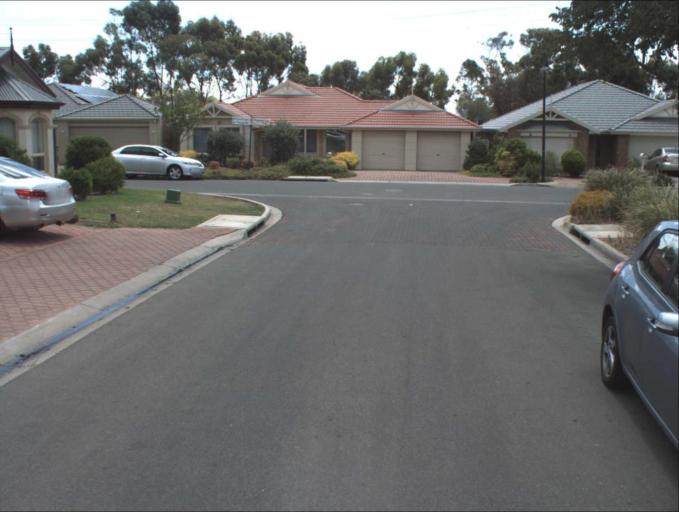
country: AU
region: South Australia
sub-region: Salisbury
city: Ingle Farm
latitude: -34.8481
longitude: 138.6305
